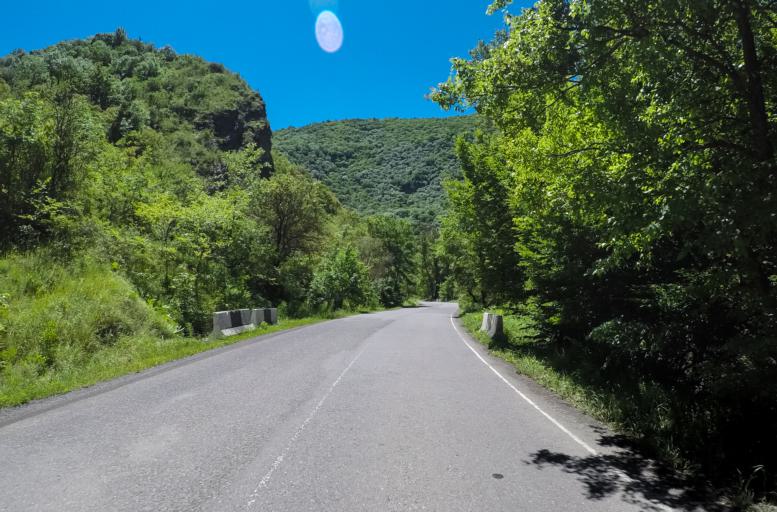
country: GE
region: Samtskhe-Javakheti
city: Akhaltsikhe
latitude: 41.6109
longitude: 43.0653
